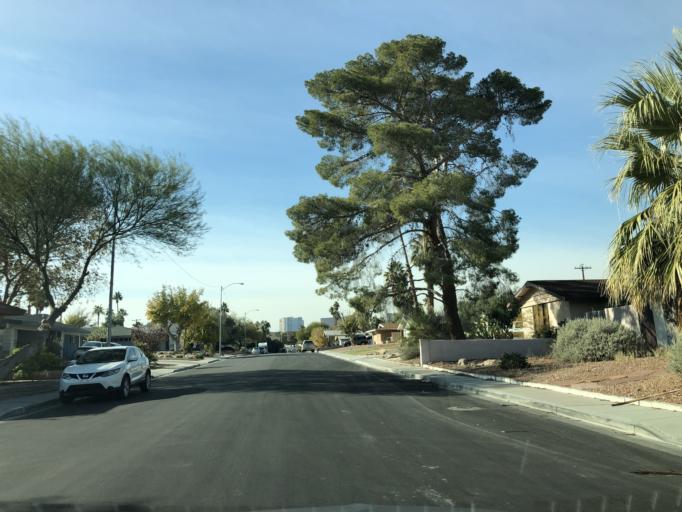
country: US
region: Nevada
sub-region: Clark County
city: Winchester
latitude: 36.1238
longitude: -115.1285
